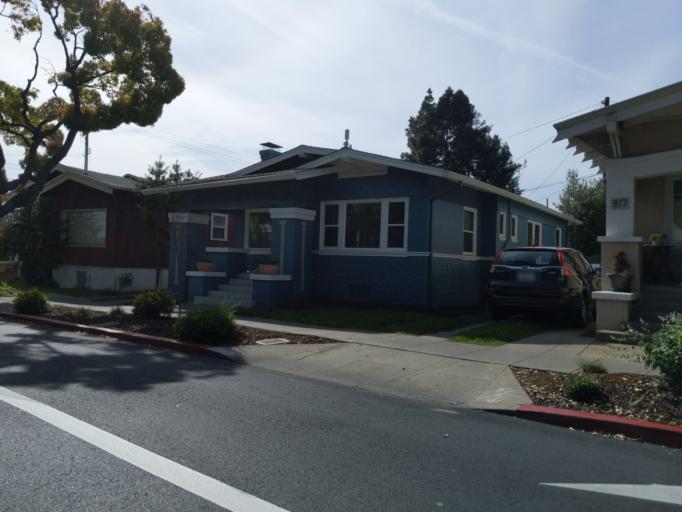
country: US
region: California
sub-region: Alameda County
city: Alameda
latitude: 37.7580
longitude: -122.2481
